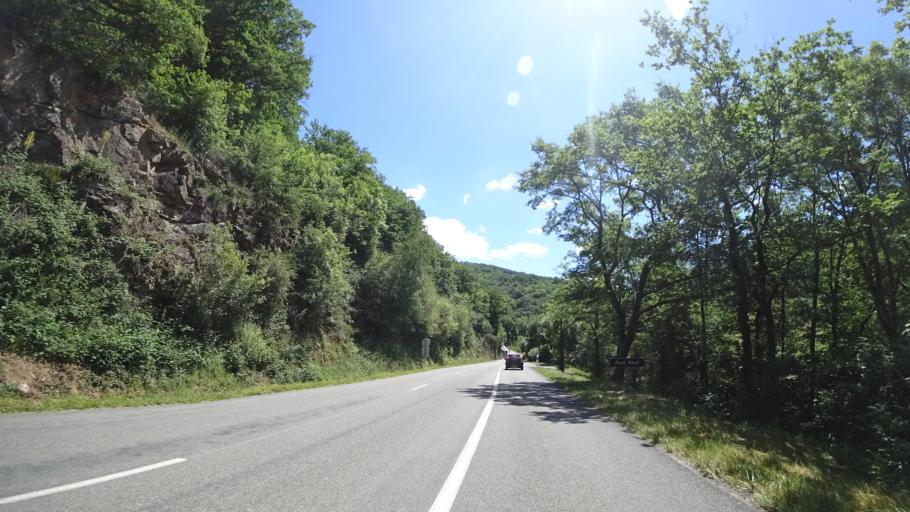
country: FR
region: Midi-Pyrenees
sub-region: Departement de l'Aveyron
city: Colombies
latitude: 44.3778
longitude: 2.3083
